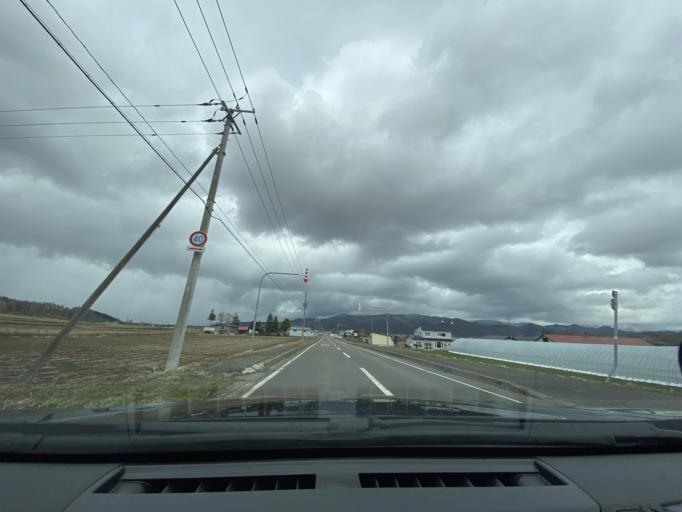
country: JP
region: Hokkaido
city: Nayoro
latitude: 44.1065
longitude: 142.4775
